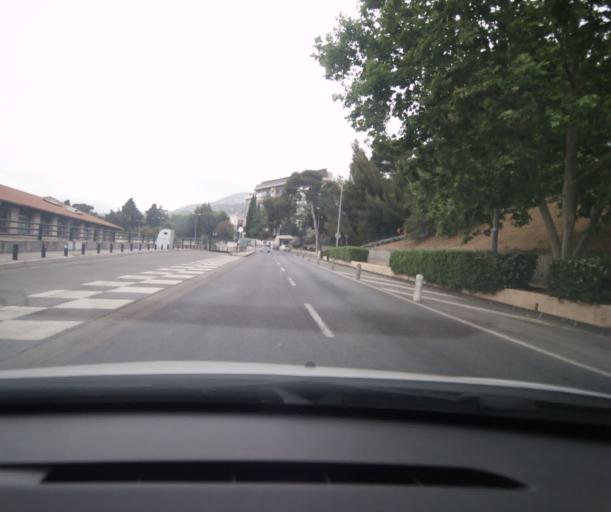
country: FR
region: Provence-Alpes-Cote d'Azur
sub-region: Departement du Var
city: Toulon
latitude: 43.1281
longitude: 5.9347
